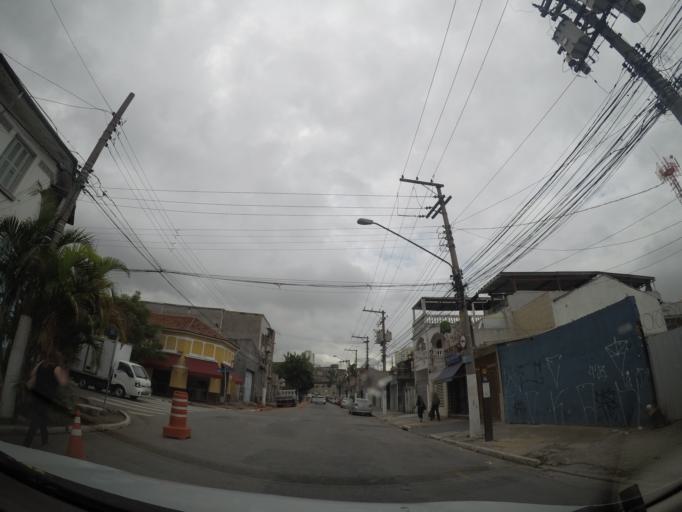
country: BR
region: Sao Paulo
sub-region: Sao Paulo
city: Sao Paulo
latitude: -23.5522
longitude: -46.6033
